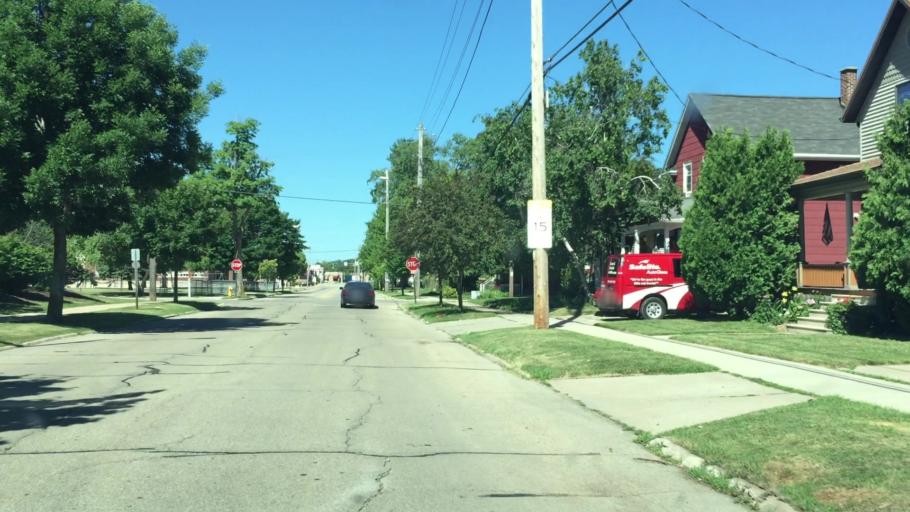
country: US
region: Wisconsin
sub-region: Winnebago County
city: Neenah
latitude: 44.1903
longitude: -88.4515
